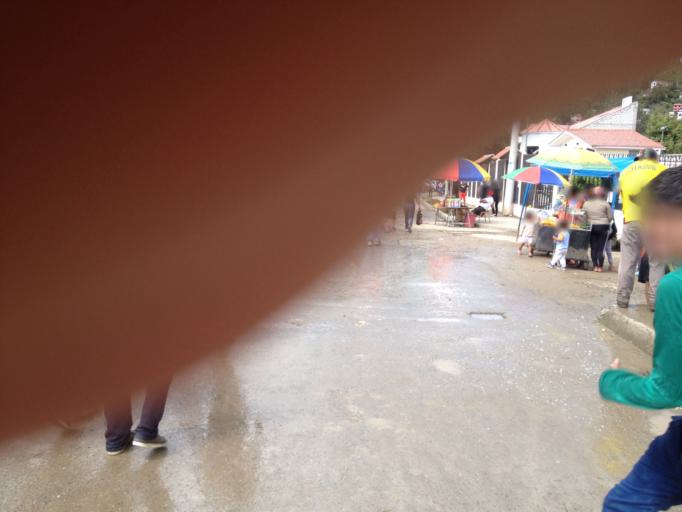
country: EC
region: Azuay
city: Gualaceo
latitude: -2.8953
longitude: -78.7750
